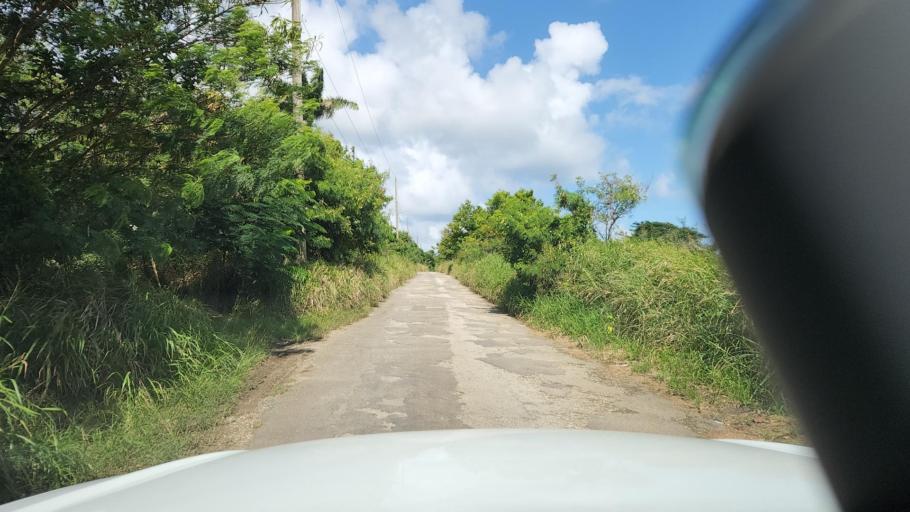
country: BB
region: Saint John
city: Four Cross Roads
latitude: 13.1683
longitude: -59.5024
